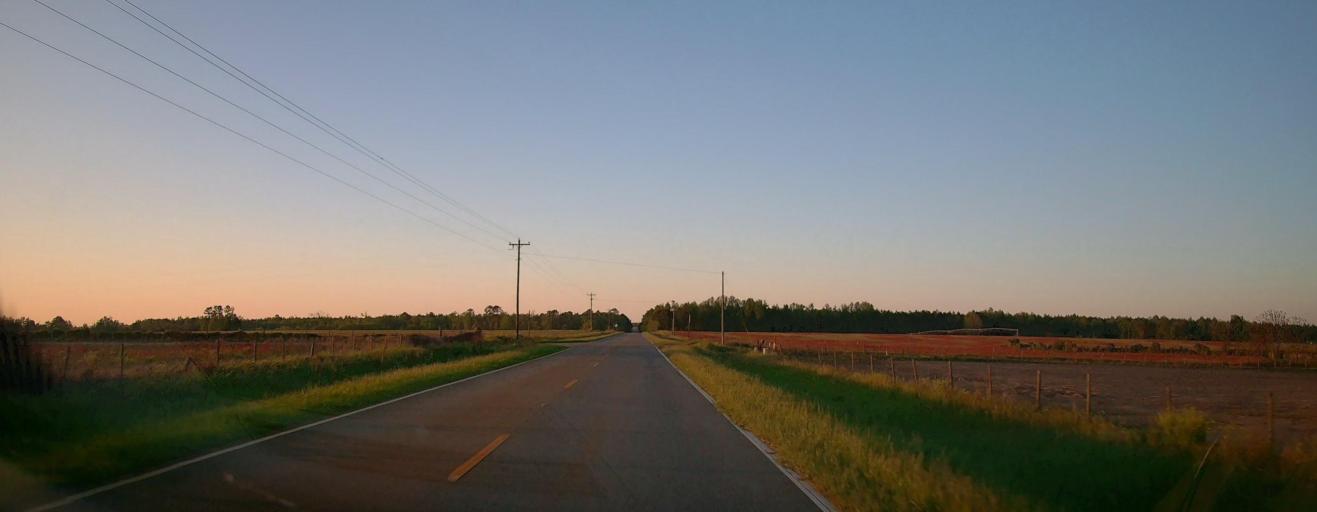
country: US
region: Georgia
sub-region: Ben Hill County
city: Fitzgerald
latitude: 31.7304
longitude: -83.3098
